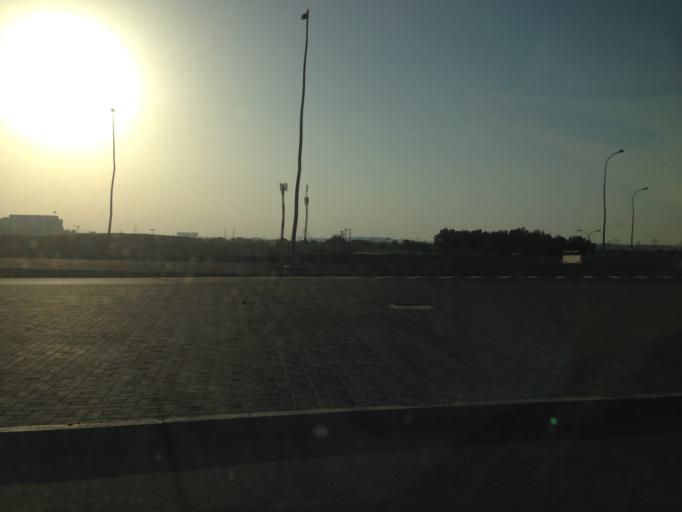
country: OM
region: Muhafazat Masqat
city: Bawshar
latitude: 23.5902
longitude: 58.3327
